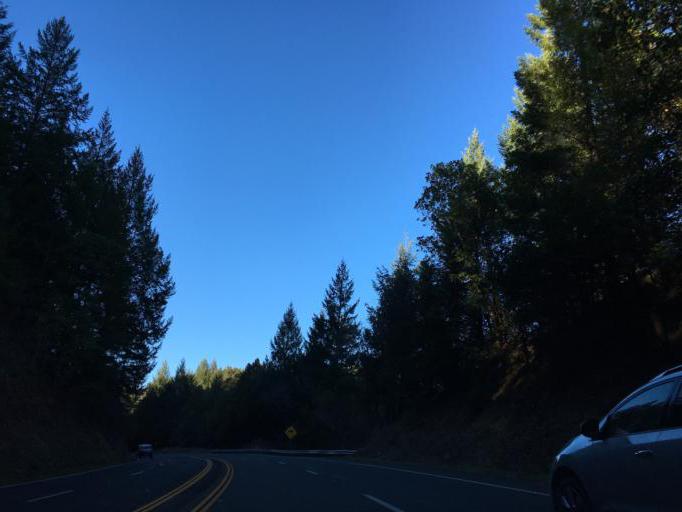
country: US
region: California
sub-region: Mendocino County
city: Brooktrails
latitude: 39.5397
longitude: -123.4177
